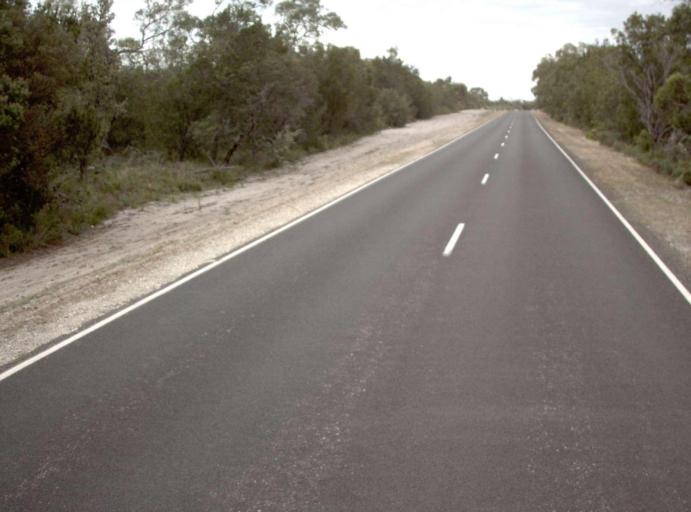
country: AU
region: Victoria
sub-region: Wellington
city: Sale
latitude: -38.1774
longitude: 147.3798
